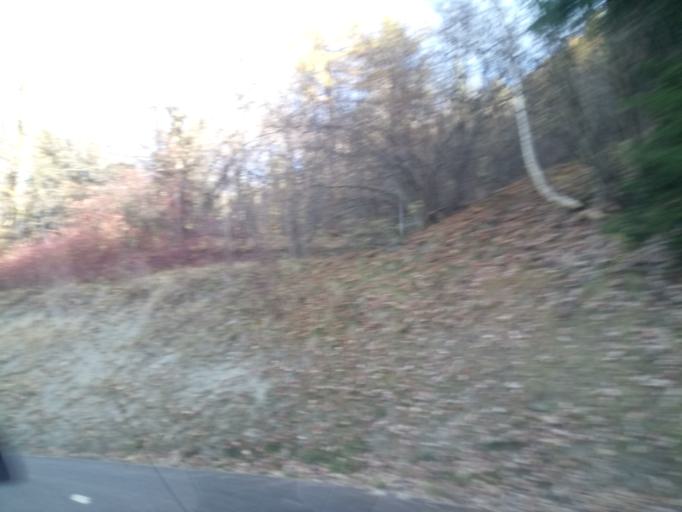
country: FR
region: Rhone-Alpes
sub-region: Departement de la Savoie
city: Saint-Michel-de-Maurienne
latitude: 45.2284
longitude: 6.4824
